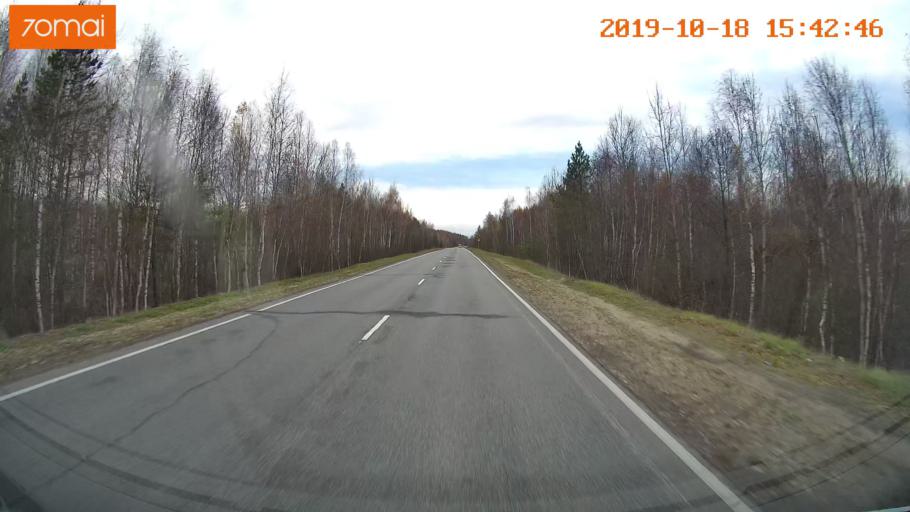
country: RU
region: Vladimir
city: Golovino
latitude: 55.9589
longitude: 40.5625
